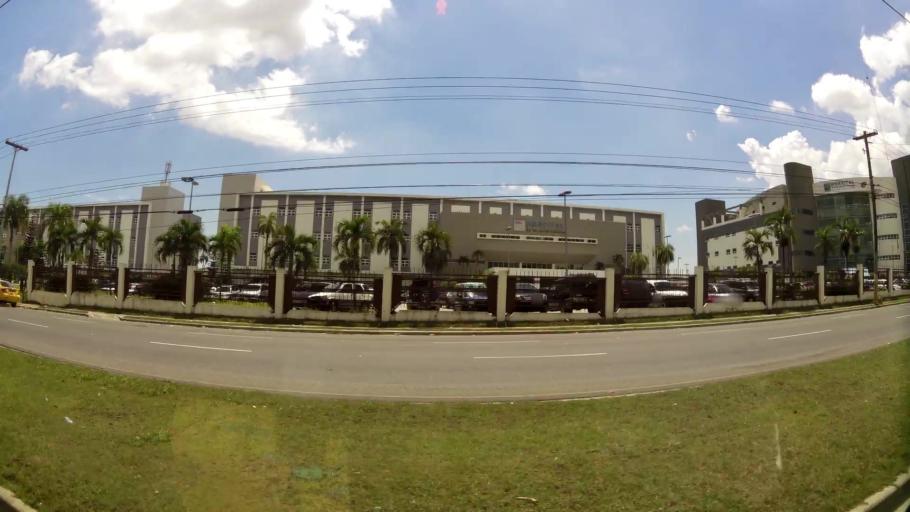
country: DO
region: Nacional
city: Ensanche Luperon
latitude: 18.5474
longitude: -69.8830
